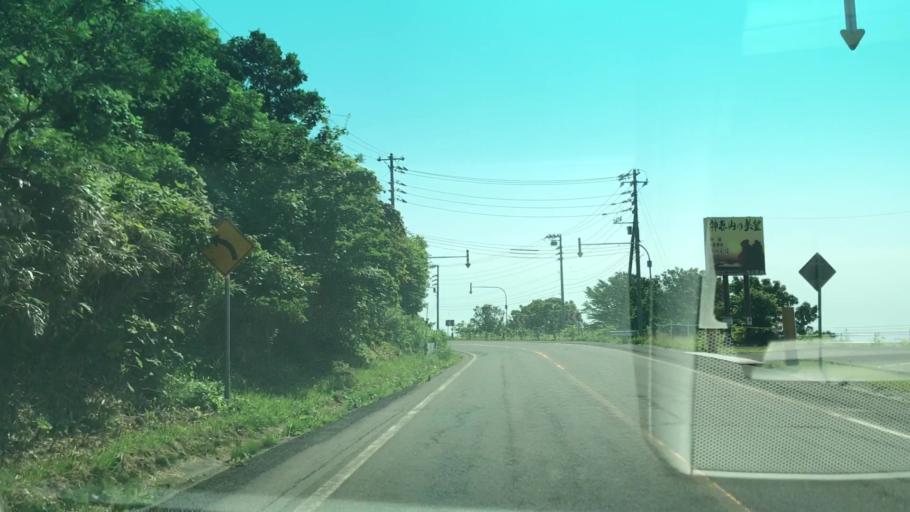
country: JP
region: Hokkaido
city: Iwanai
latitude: 43.1383
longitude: 140.4308
